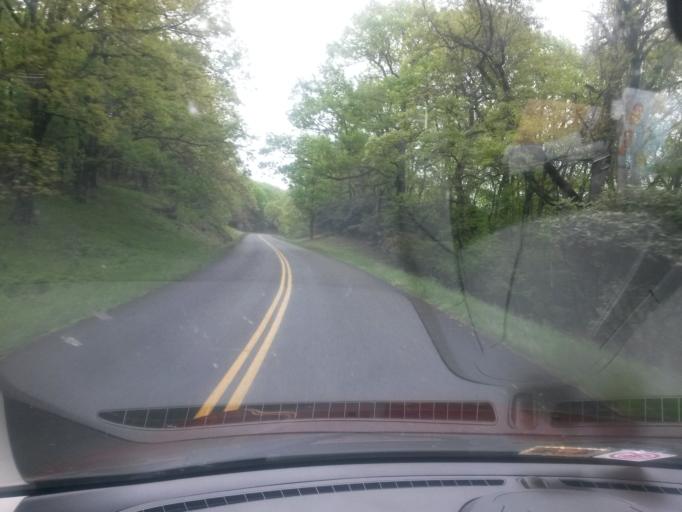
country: US
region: Virginia
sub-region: Floyd County
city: Floyd
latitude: 36.8252
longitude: -80.3465
